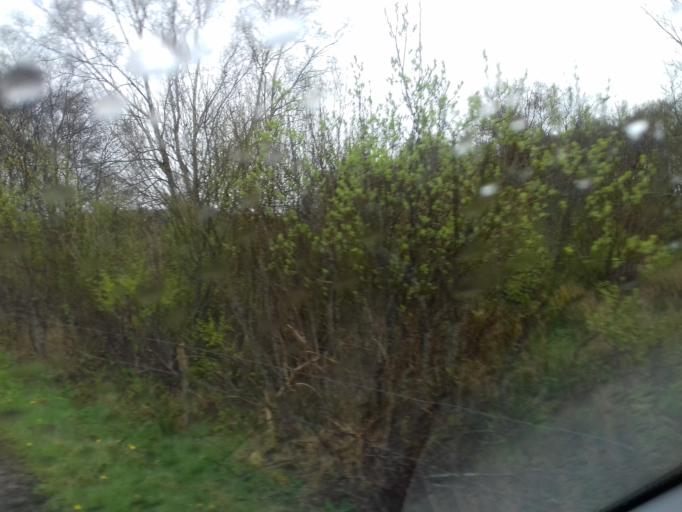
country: IE
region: Connaught
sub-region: County Leitrim
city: Manorhamilton
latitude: 54.2596
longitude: -7.9275
